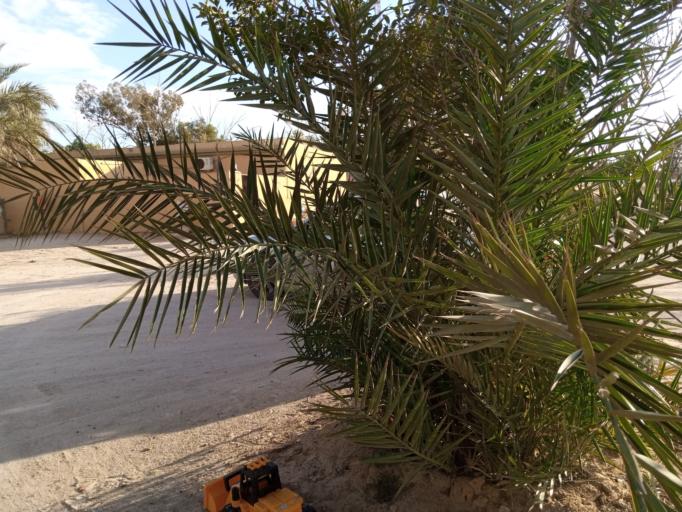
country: LY
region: Az Zawiyah
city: Zawiya
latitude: 32.6372
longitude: 12.6896
